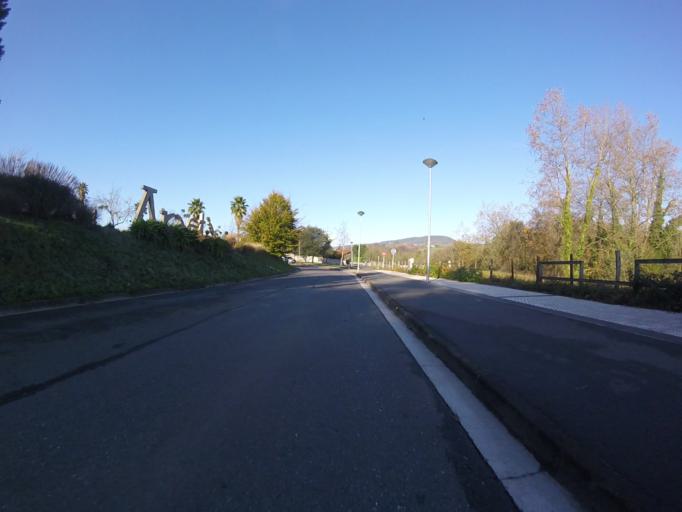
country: ES
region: Basque Country
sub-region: Provincia de Guipuzcoa
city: Lasarte
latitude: 43.2713
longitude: -2.0292
